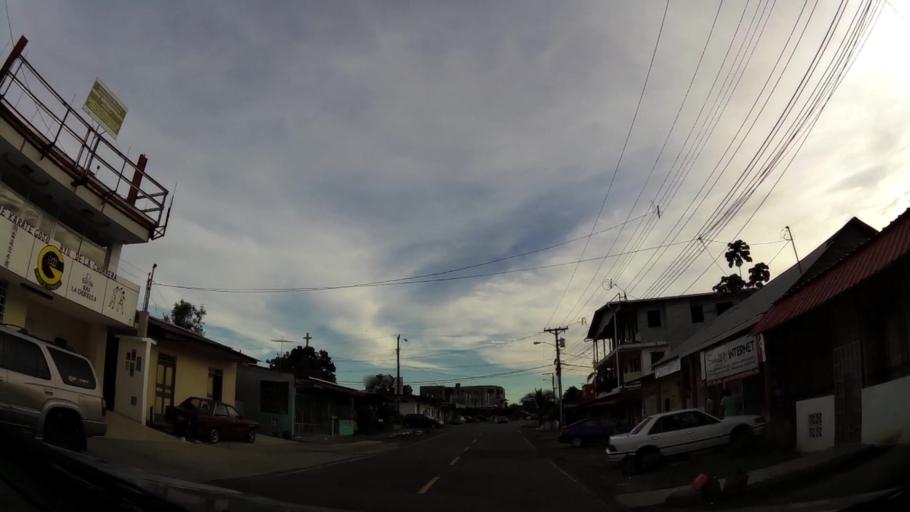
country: PA
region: Panama
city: La Chorrera
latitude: 8.8842
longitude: -79.7809
